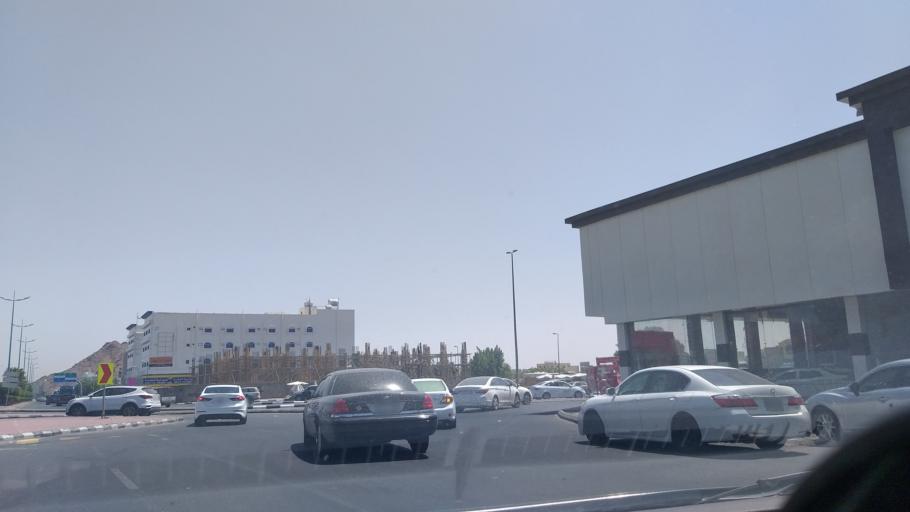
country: SA
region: Makkah
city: Ta'if
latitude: 21.2973
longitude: 40.4269
